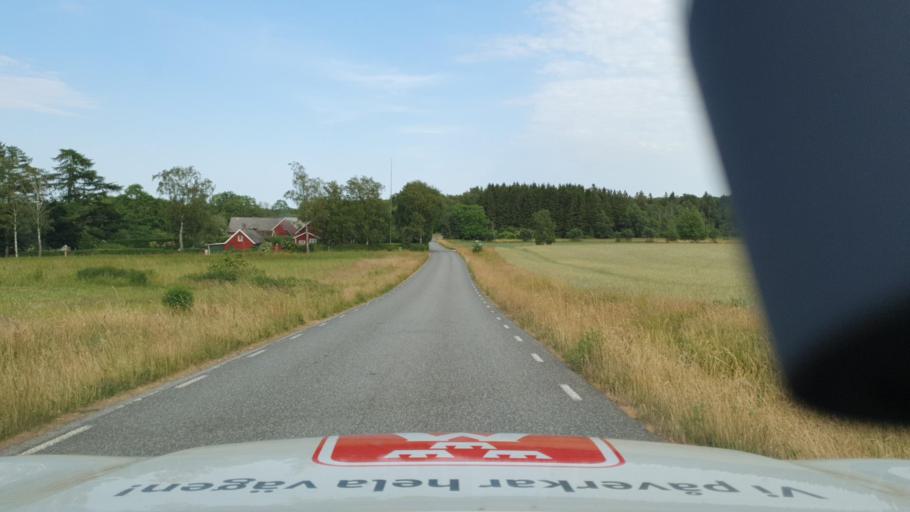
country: SE
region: Skane
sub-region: Kristianstads Kommun
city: Degeberga
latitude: 55.6901
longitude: 14.0895
